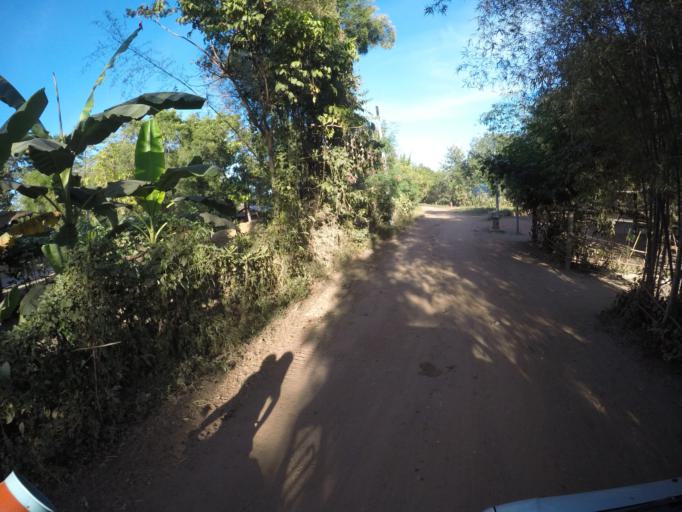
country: MM
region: Bago
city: Pyay
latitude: 18.7957
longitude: 95.3072
